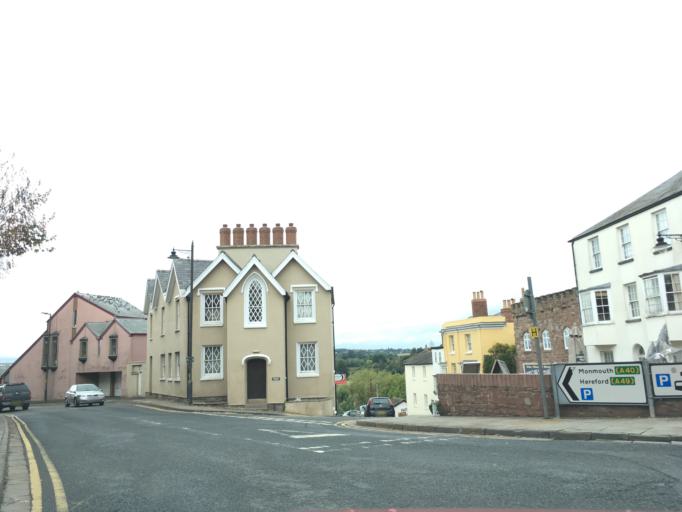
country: GB
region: England
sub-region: Herefordshire
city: Ross on Wye
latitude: 51.9147
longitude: -2.5859
